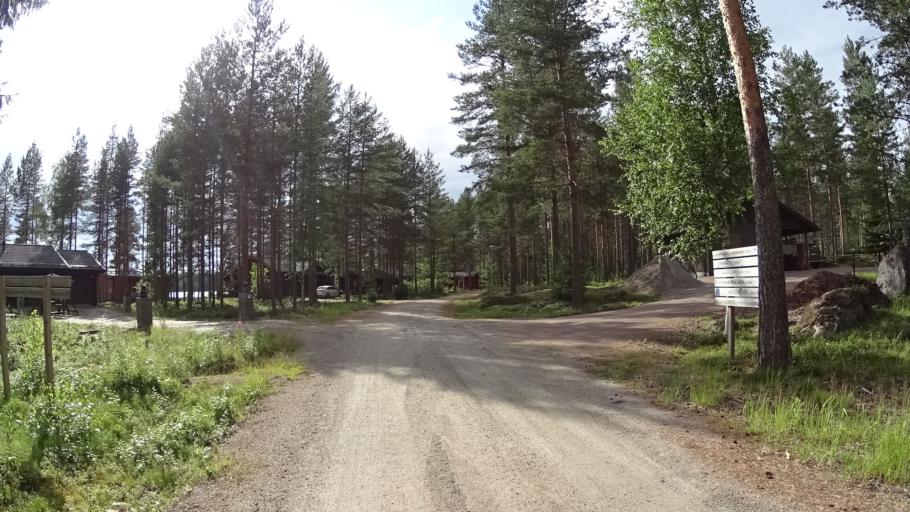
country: FI
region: Southern Ostrobothnia
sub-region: Kuusiokunnat
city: AEhtaeri
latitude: 62.5275
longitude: 24.1963
